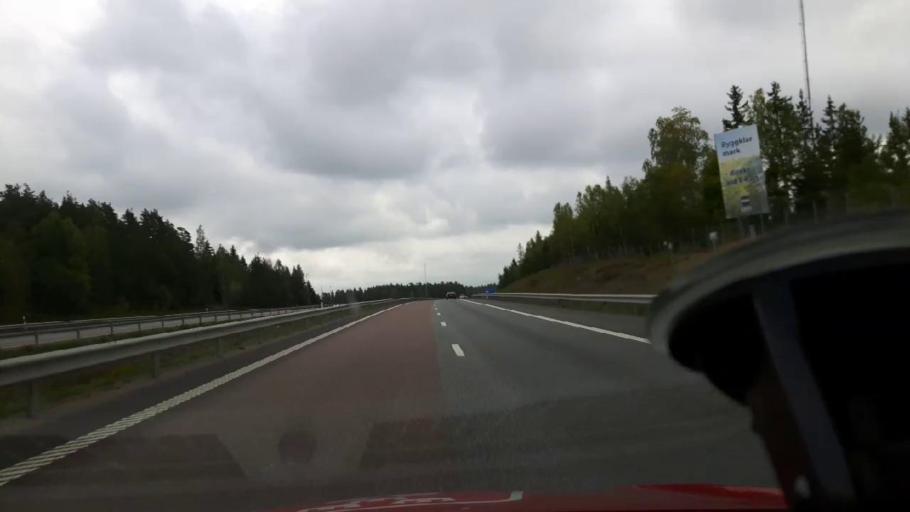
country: SE
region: Gaevleborg
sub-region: Gavle Kommun
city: Gavle
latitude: 60.6423
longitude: 17.1309
